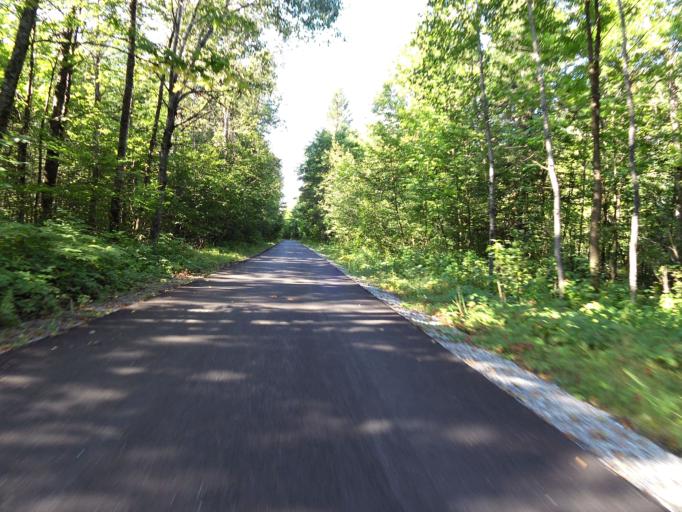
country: CA
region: Quebec
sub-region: Outaouais
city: Maniwaki
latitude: 46.2306
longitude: -76.0335
